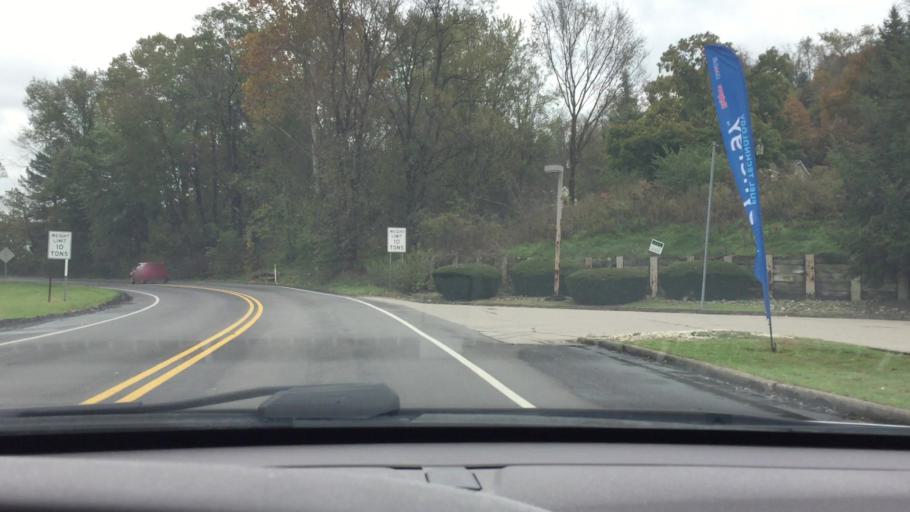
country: US
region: Pennsylvania
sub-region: Washington County
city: Speers
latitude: 40.1189
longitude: -79.8840
